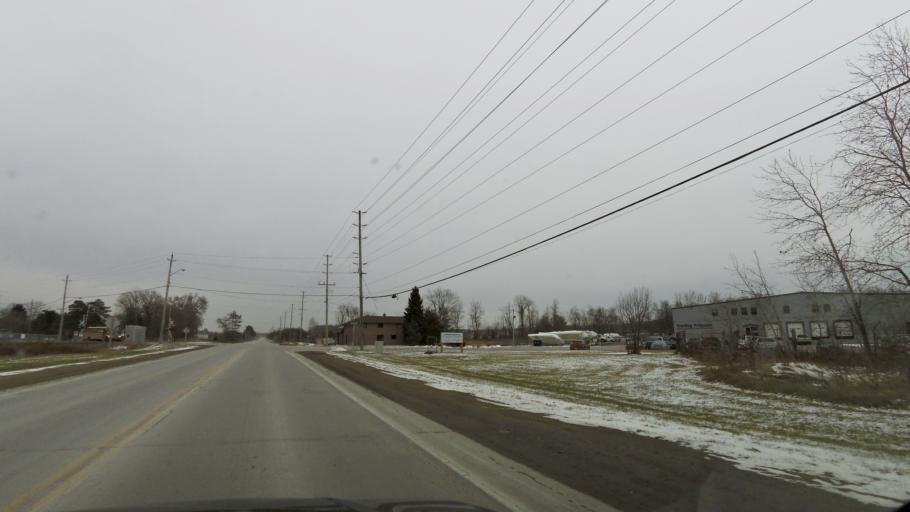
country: CA
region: Ontario
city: Newmarket
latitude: 44.1053
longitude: -79.5161
